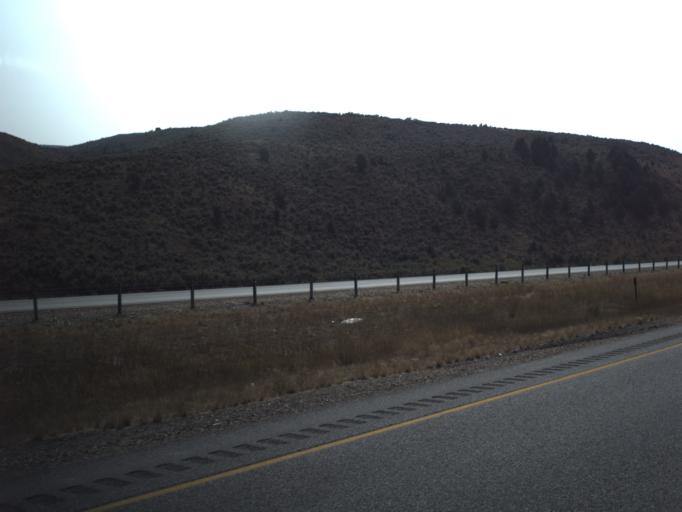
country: US
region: Utah
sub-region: Summit County
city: Coalville
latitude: 41.0897
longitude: -111.2275
